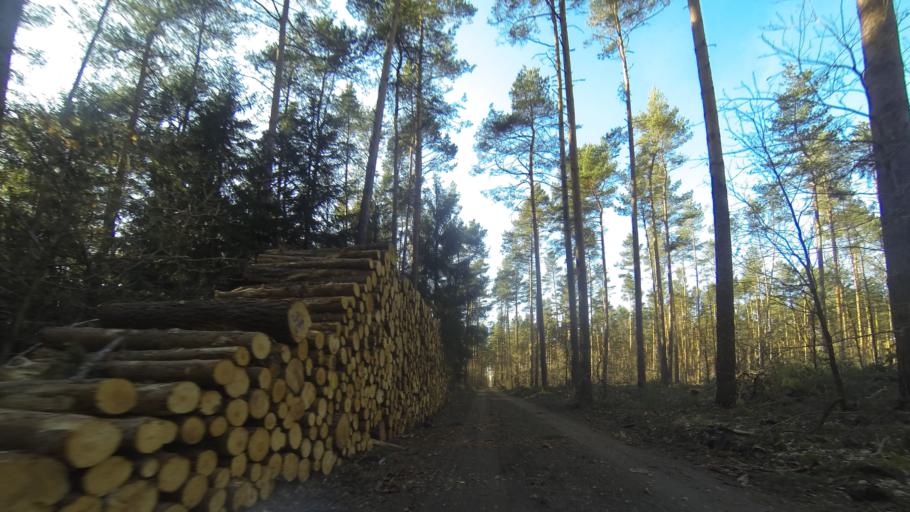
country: DE
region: Saxony
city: Laussnitz
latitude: 51.2616
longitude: 13.8523
